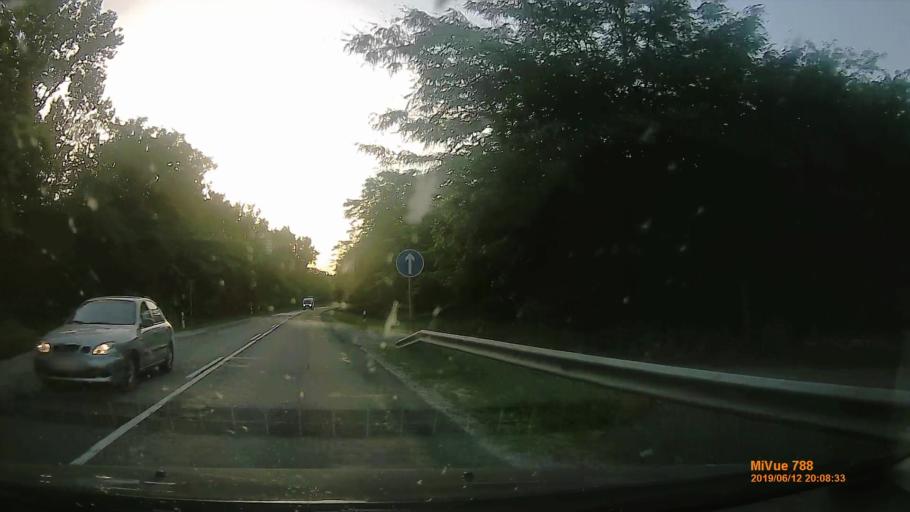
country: HU
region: Pest
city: Ocsa
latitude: 47.2475
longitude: 19.2334
